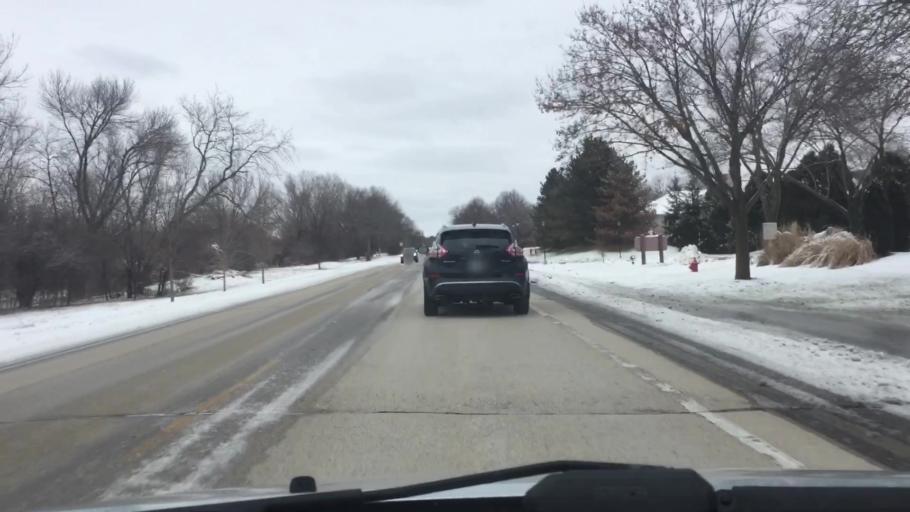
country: US
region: Wisconsin
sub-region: Waukesha County
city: Brookfield
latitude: 43.0409
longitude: -88.1062
